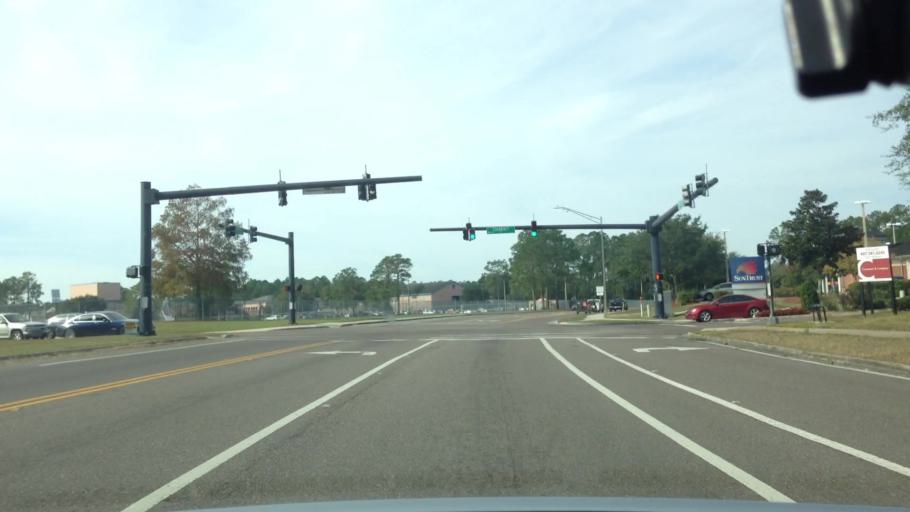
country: US
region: Florida
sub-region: Nassau County
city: Yulee
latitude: 30.4838
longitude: -81.6036
